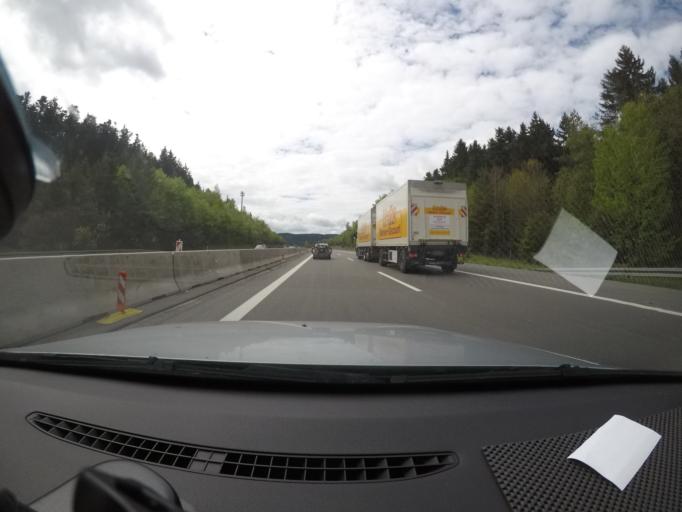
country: DE
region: Baden-Wuerttemberg
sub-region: Freiburg Region
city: Vohringen
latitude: 48.3057
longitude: 8.6361
